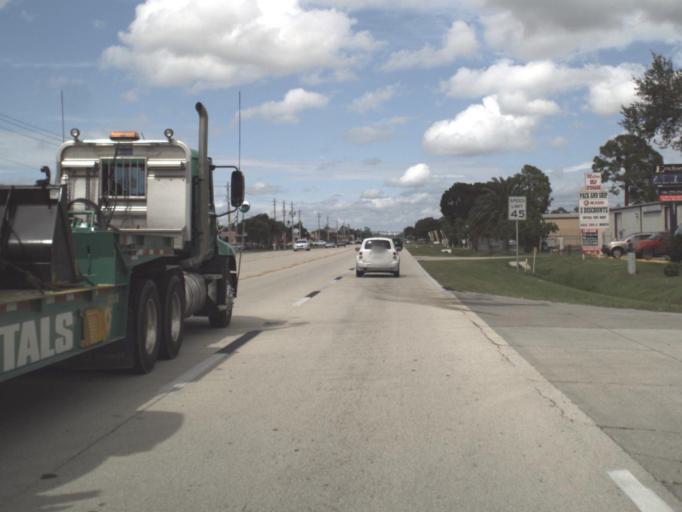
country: US
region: Florida
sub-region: Lee County
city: Villas
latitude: 26.5586
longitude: -81.8529
